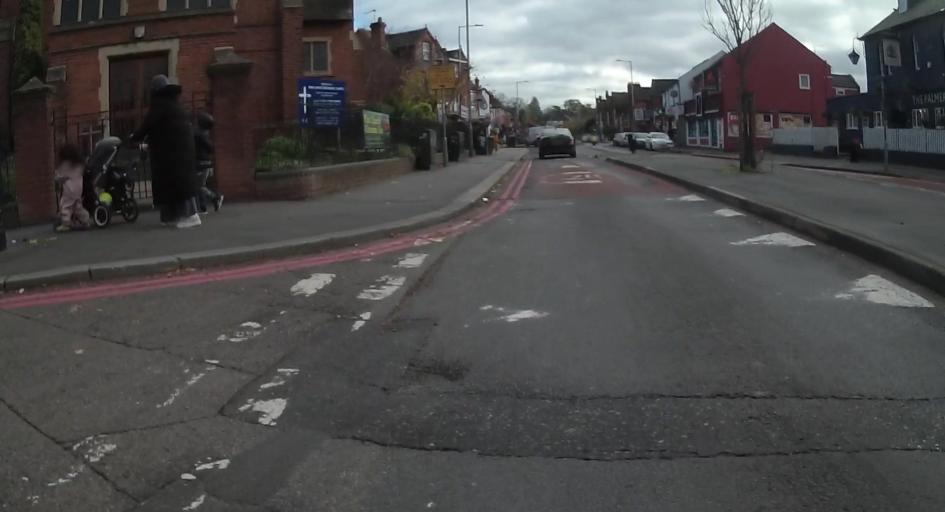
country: GB
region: England
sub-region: Wokingham
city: Earley
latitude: 51.4505
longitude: -0.9382
